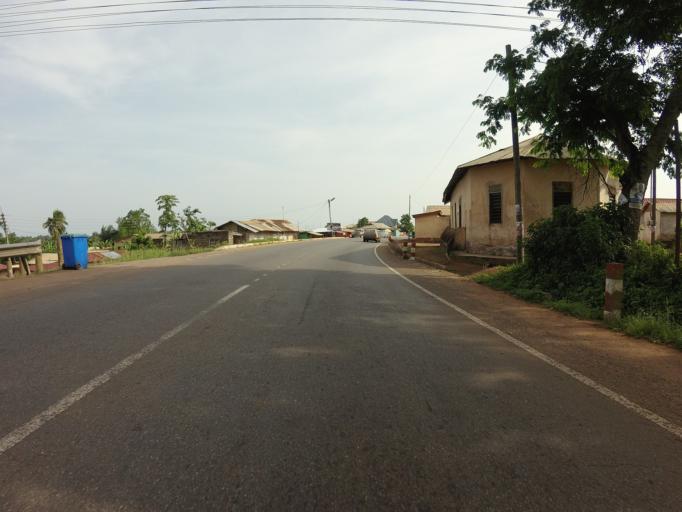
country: GH
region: Eastern
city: Aburi
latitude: 5.8623
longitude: -0.1647
